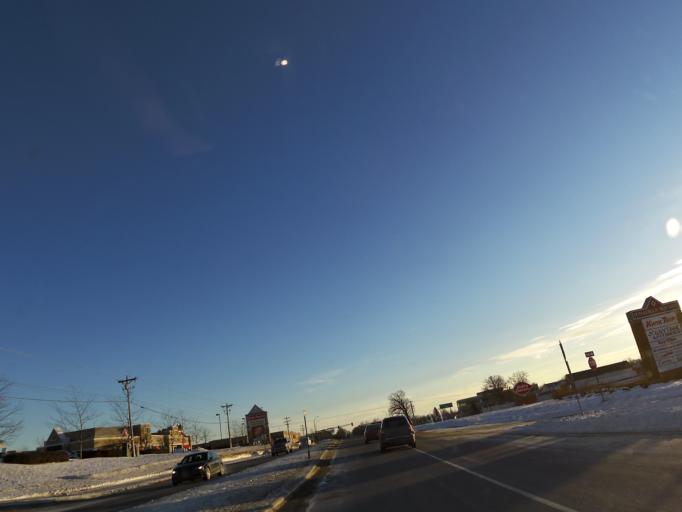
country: US
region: Minnesota
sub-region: Carver County
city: Chaska
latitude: 44.8307
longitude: -93.6024
